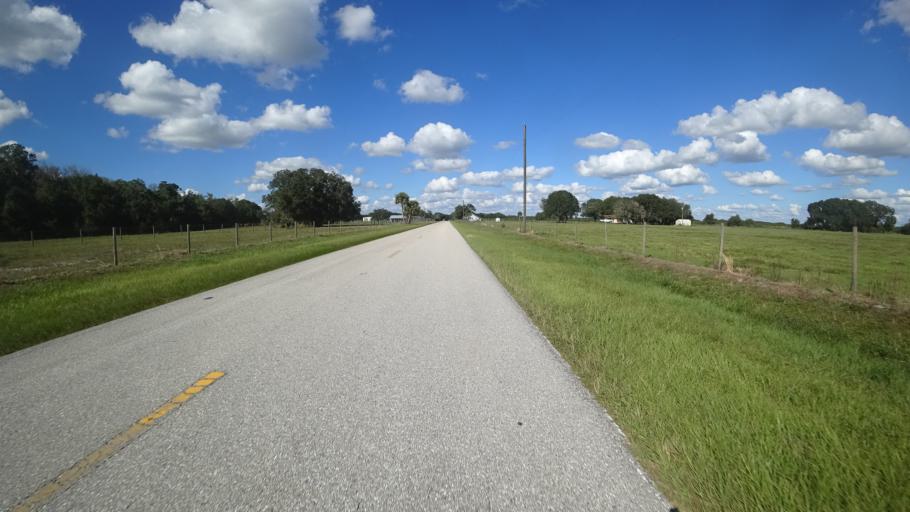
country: US
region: Florida
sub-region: Sarasota County
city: North Port
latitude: 27.2025
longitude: -82.1222
